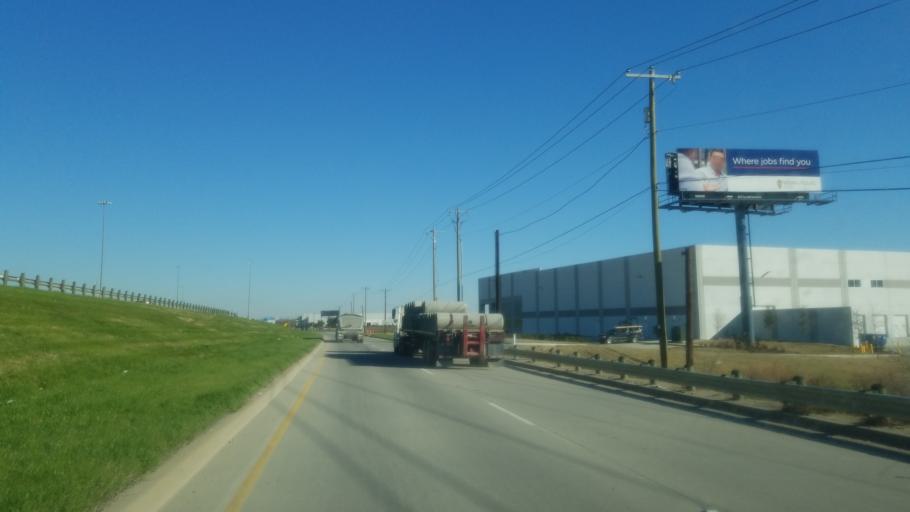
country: US
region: Texas
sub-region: Dallas County
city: Grand Prairie
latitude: 32.7617
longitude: -96.9521
